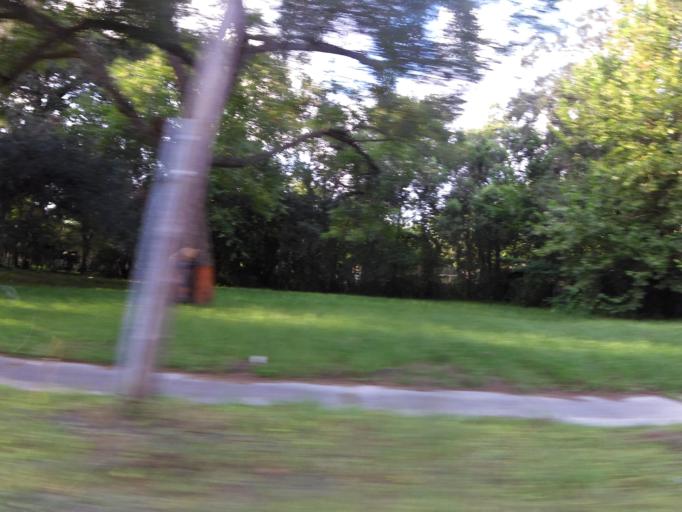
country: US
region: Florida
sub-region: Duval County
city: Jacksonville
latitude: 30.3259
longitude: -81.7029
